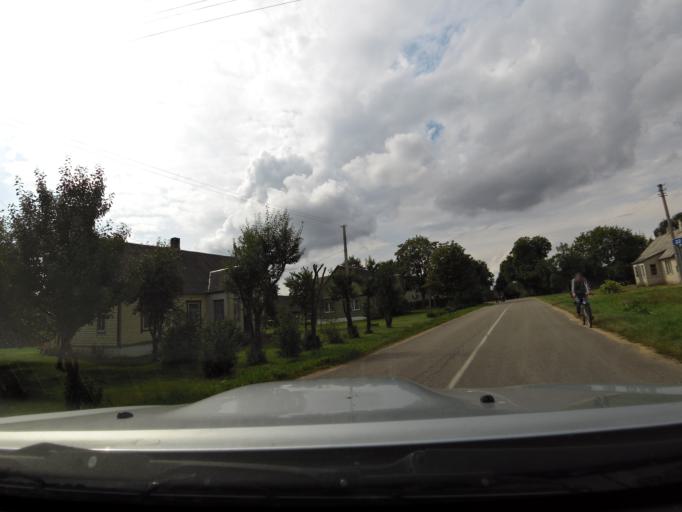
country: LT
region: Vilnius County
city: Elektrenai
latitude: 54.9025
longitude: 24.7266
